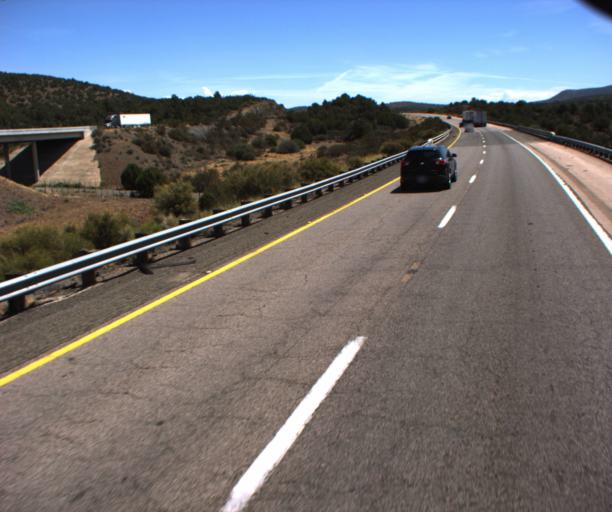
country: US
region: Arizona
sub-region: Mohave County
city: Peach Springs
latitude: 35.1891
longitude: -113.3177
